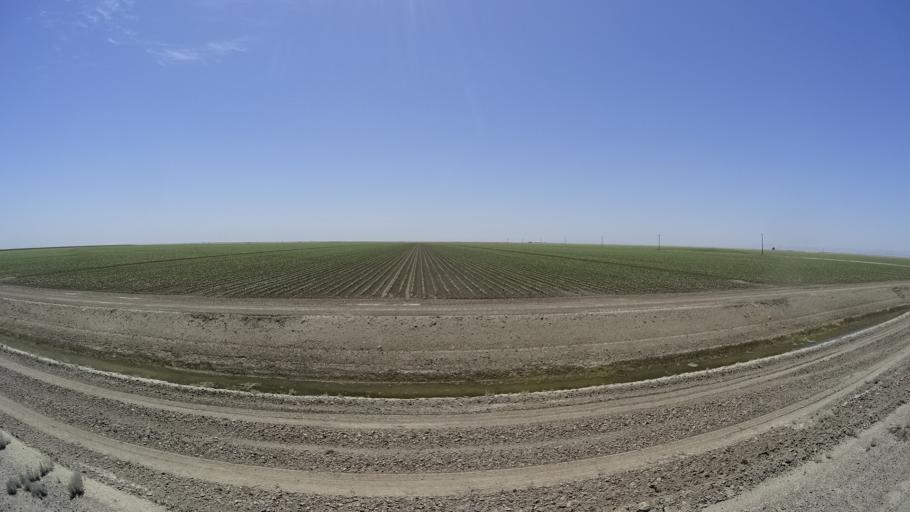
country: US
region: California
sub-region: Kings County
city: Corcoran
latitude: 36.1161
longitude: -119.6696
